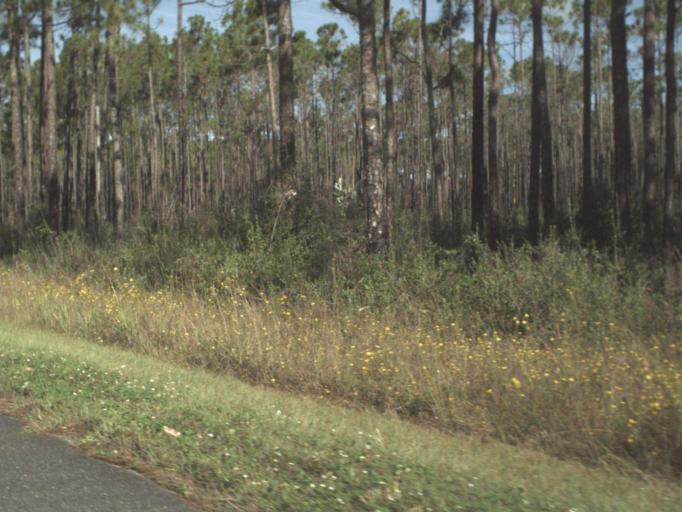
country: US
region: Florida
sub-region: Franklin County
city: Eastpoint
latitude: 29.8270
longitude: -84.9167
